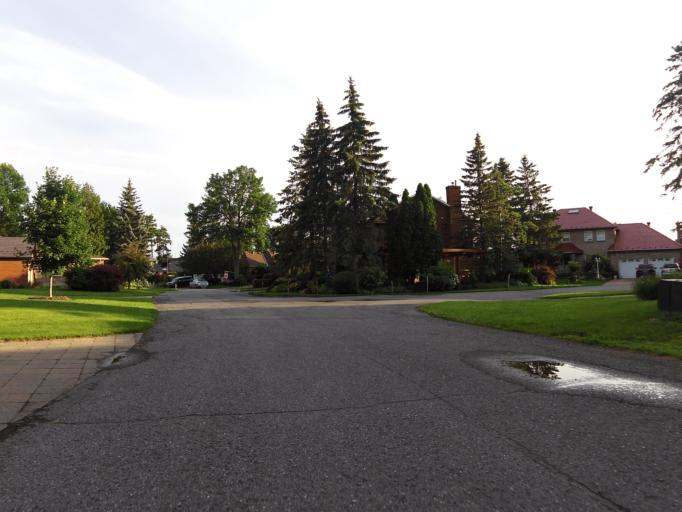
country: CA
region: Ontario
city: Bells Corners
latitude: 45.3494
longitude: -75.8166
